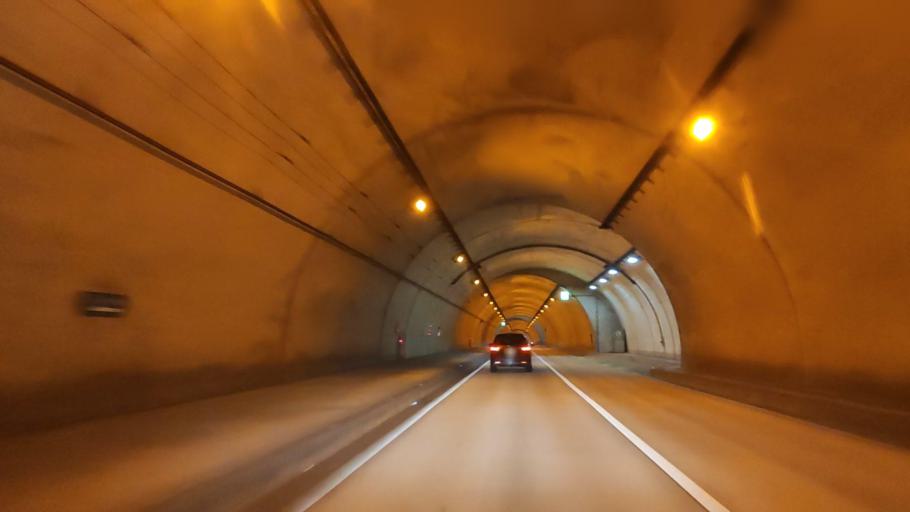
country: JP
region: Ehime
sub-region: Shikoku-chuo Shi
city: Matsuyama
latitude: 33.8804
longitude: 132.7115
